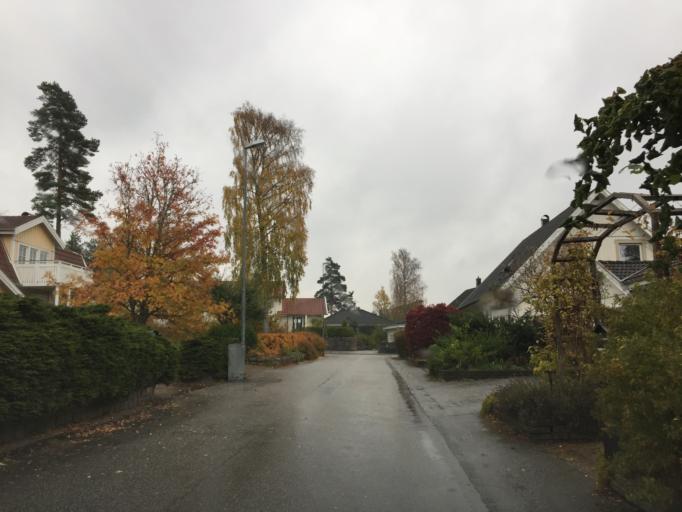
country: SE
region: Vaestra Goetaland
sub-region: Trollhattan
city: Trollhattan
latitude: 58.3255
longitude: 12.2717
